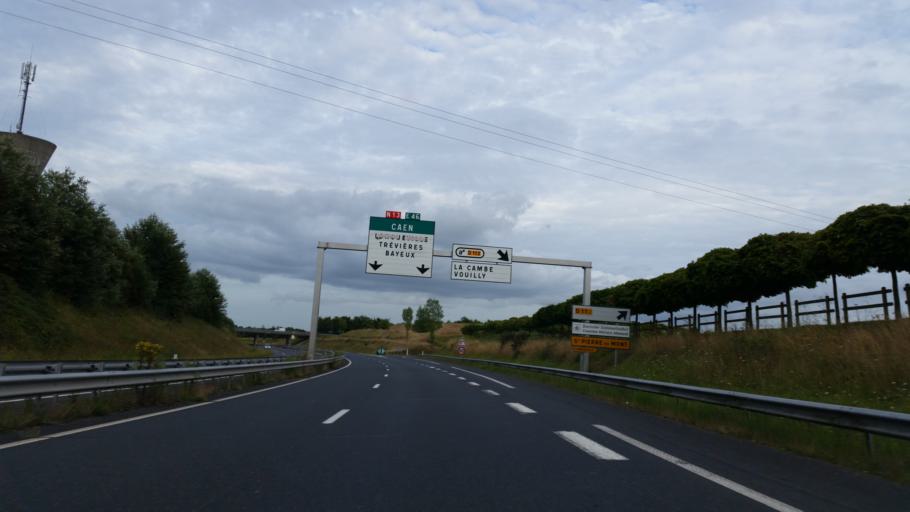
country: FR
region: Lower Normandy
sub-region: Departement du Calvados
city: Grandcamp-Maisy
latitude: 49.3388
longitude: -1.0116
